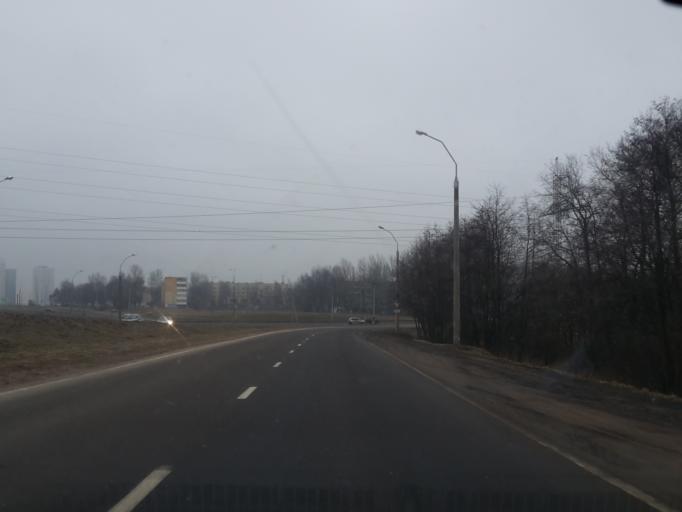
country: BY
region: Minsk
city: Zhdanovichy
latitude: 53.9107
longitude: 27.4064
